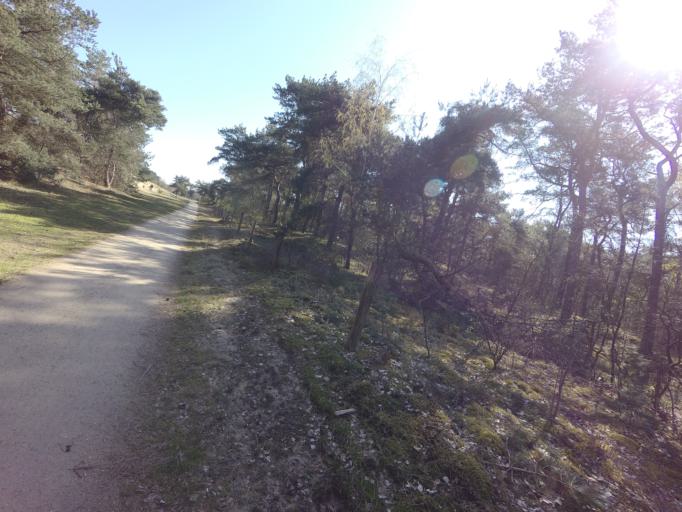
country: NL
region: Limburg
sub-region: Gemeente Bergen
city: Wellerlooi
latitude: 51.5989
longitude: 6.0738
